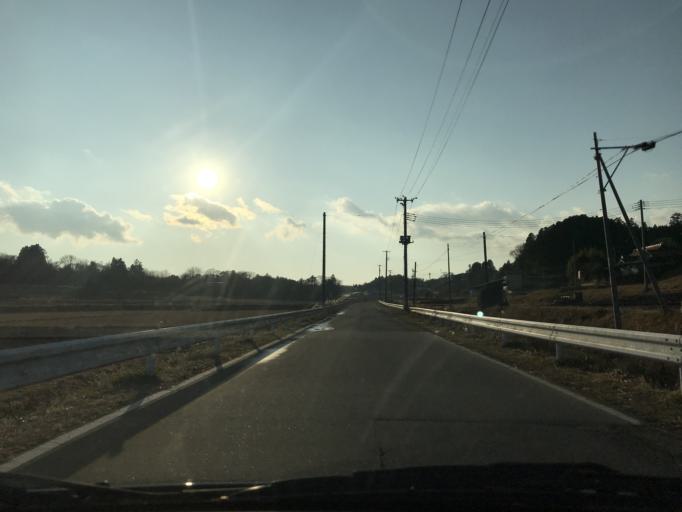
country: JP
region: Miyagi
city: Wakuya
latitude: 38.7008
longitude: 141.1170
